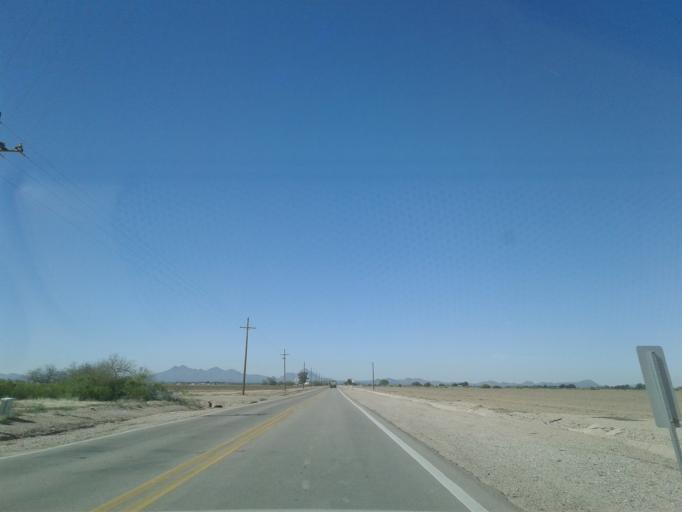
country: US
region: Arizona
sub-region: Pima County
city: Marana
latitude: 32.4605
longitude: -111.2341
